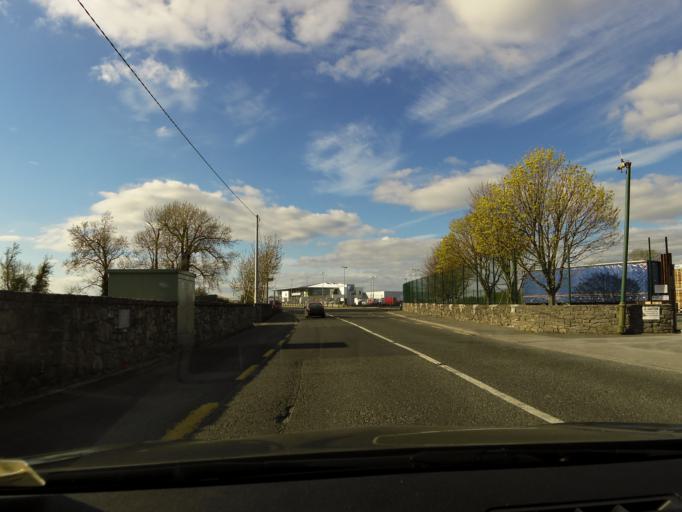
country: IE
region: Connaught
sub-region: County Galway
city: Portumna
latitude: 53.0971
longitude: -8.2255
